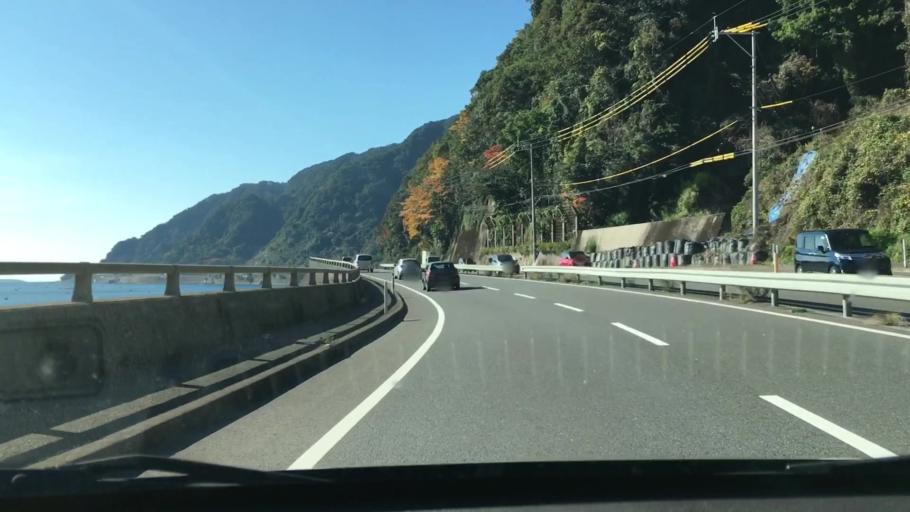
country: JP
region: Kagoshima
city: Kajiki
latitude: 31.6534
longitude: 130.6088
